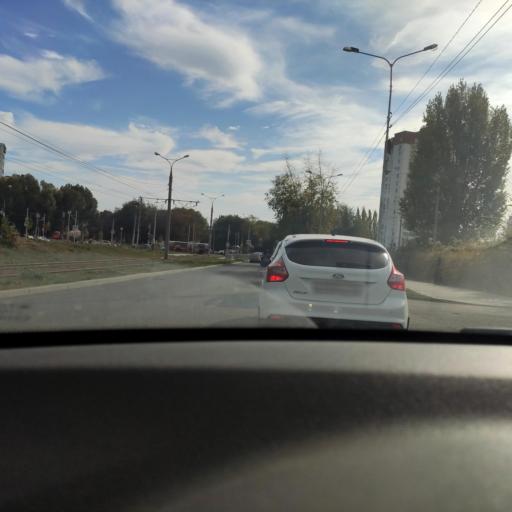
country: RU
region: Samara
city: Samara
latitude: 53.2497
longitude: 50.2470
